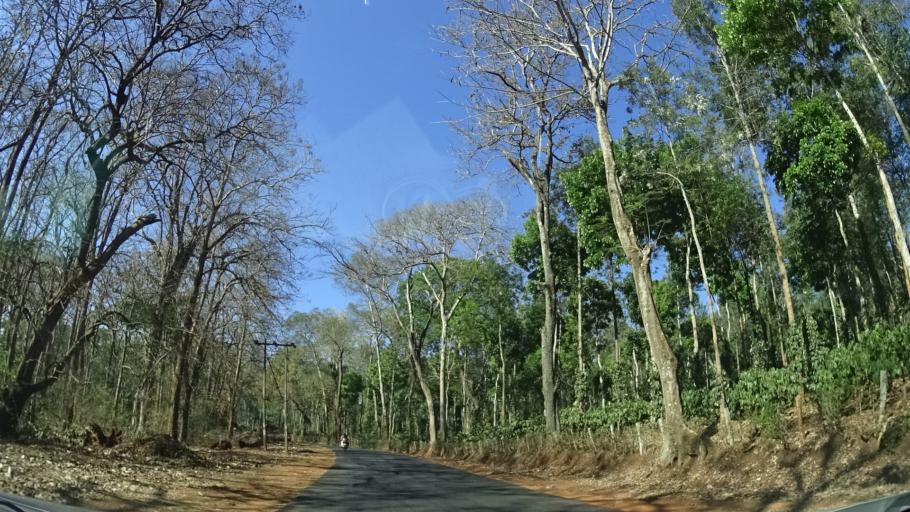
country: IN
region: Karnataka
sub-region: Chikmagalur
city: Koppa
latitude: 13.3505
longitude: 75.4844
